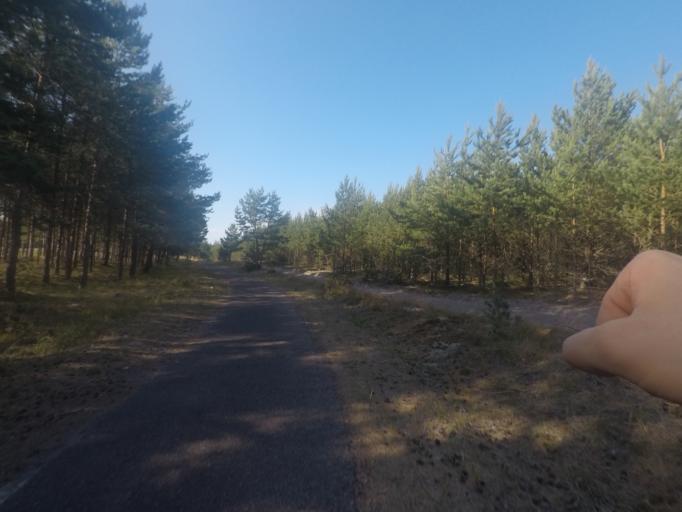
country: LT
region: Klaipedos apskritis
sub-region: Klaipeda
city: Klaipeda
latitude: 55.5722
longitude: 21.1139
